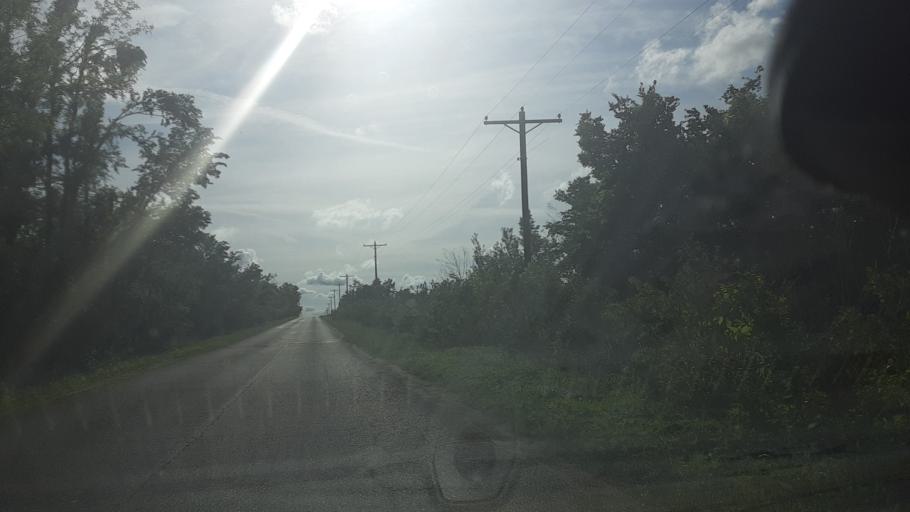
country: US
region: Oklahoma
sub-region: Logan County
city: Guthrie
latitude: 36.0576
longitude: -97.4026
